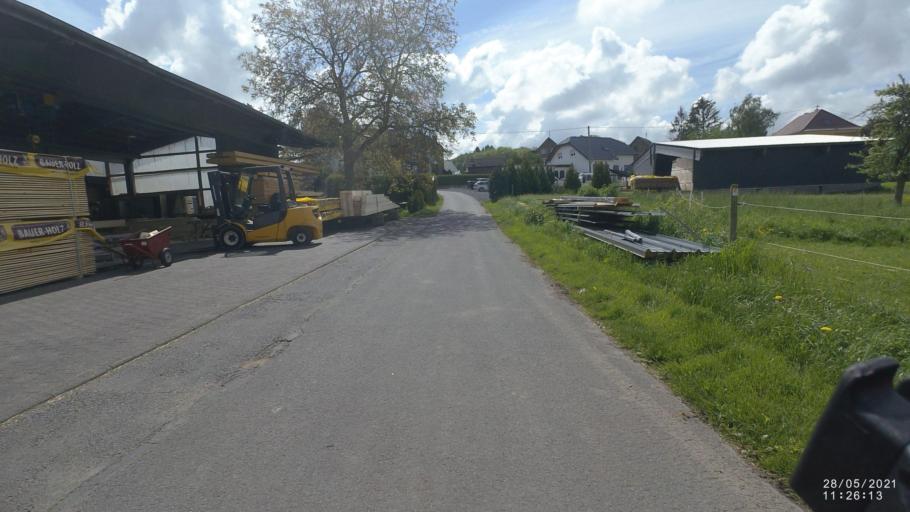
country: DE
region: Rheinland-Pfalz
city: Wierschem
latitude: 50.2249
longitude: 7.3488
